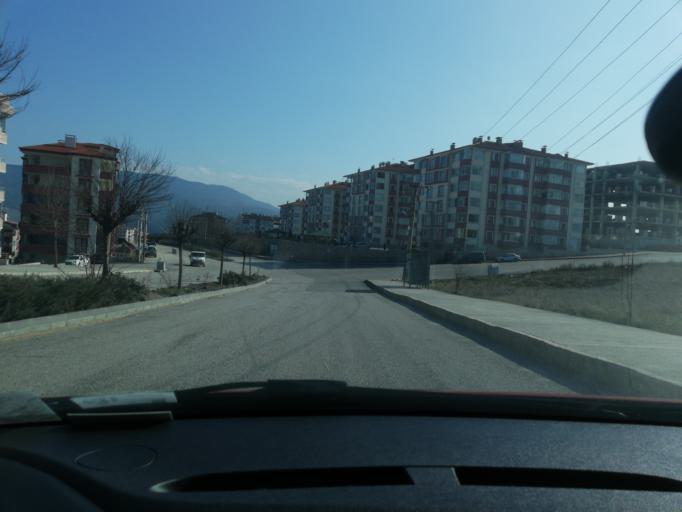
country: TR
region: Karabuk
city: Safranbolu
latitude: 41.2365
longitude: 32.6649
